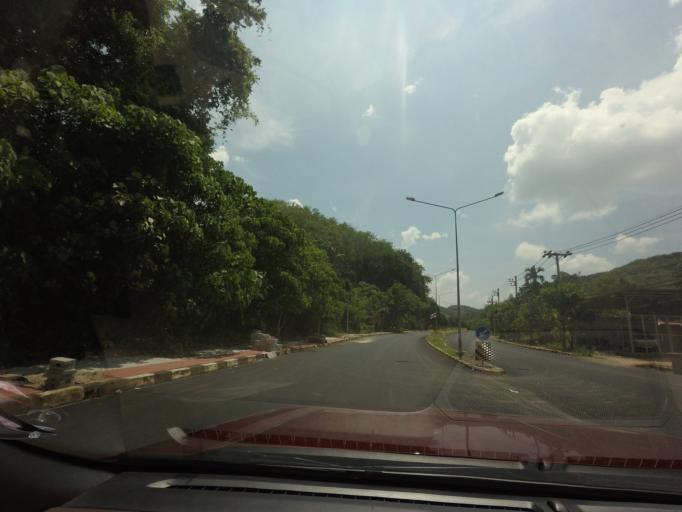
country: TH
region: Yala
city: Betong
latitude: 5.7564
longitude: 101.0442
